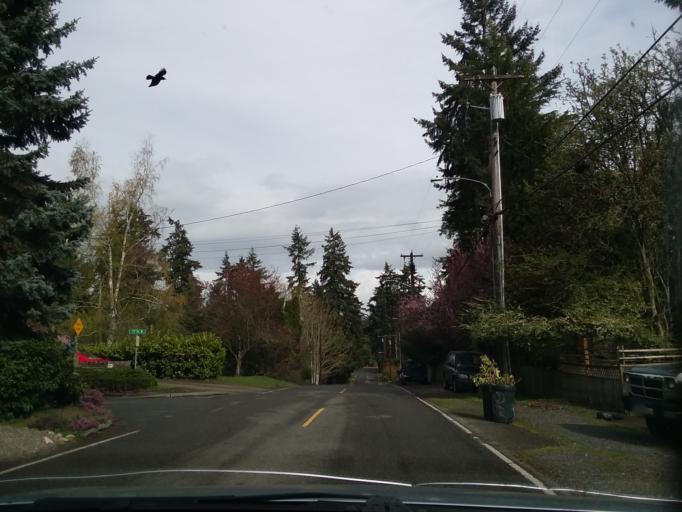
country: US
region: Washington
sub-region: Snohomish County
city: Esperance
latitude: 47.7869
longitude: -122.3384
